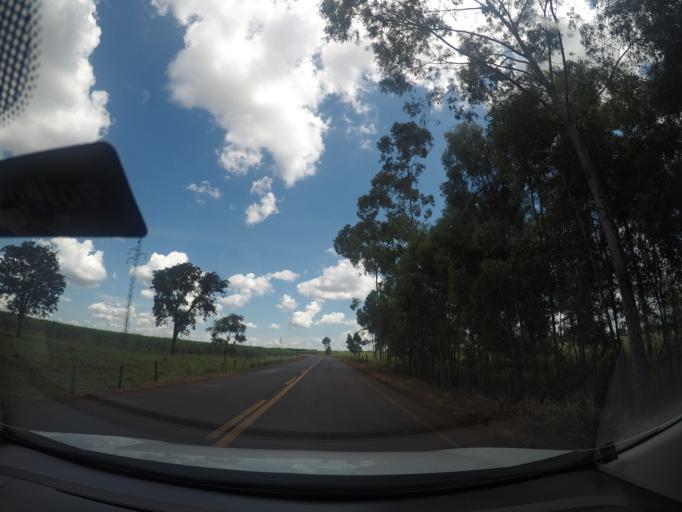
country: BR
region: Minas Gerais
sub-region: Frutal
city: Frutal
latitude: -19.8436
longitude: -48.7373
